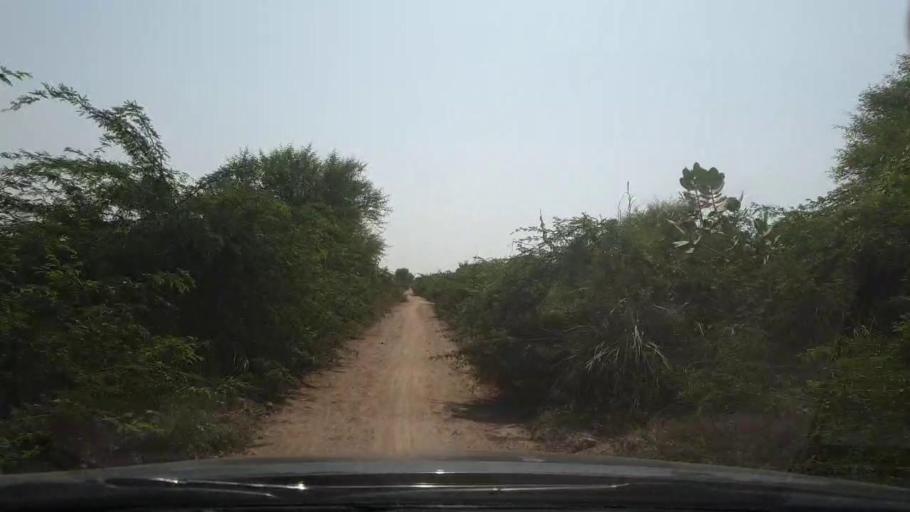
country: PK
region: Sindh
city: Naukot
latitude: 24.8081
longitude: 69.2596
